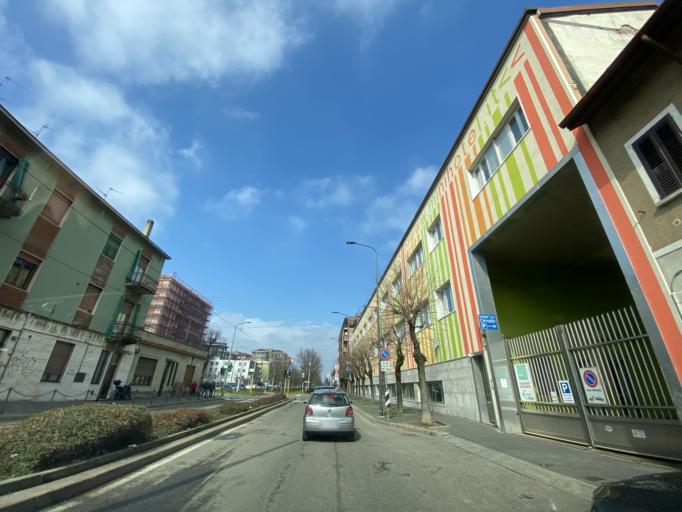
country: IT
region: Lombardy
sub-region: Citta metropolitana di Milano
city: Bresso
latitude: 45.5193
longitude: 9.1921
